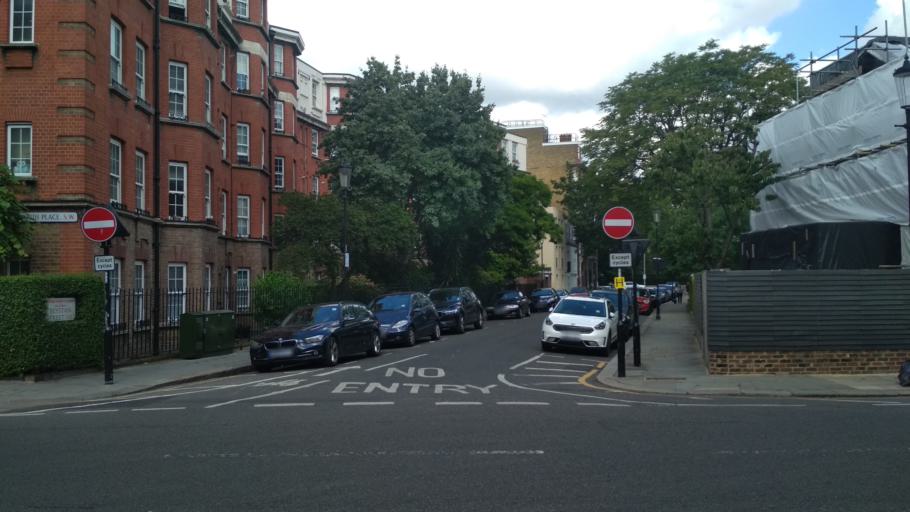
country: GB
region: England
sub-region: Greater London
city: Chelsea
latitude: 51.4922
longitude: -0.1684
